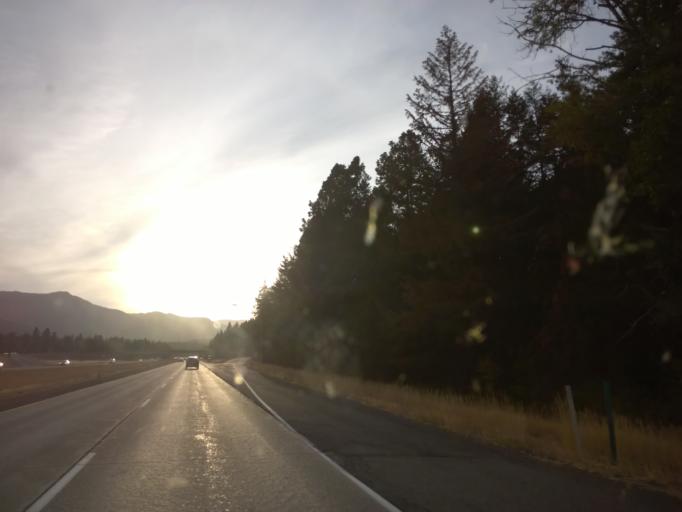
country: US
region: Washington
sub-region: Kittitas County
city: Cle Elum
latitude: 47.1842
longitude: -121.0098
